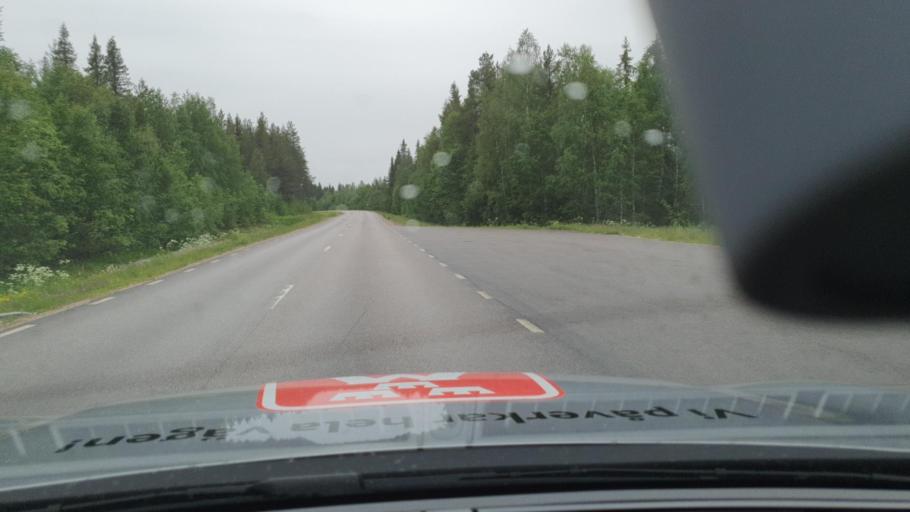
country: SE
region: Norrbotten
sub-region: Overtornea Kommun
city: OEvertornea
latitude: 66.4056
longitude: 23.4765
